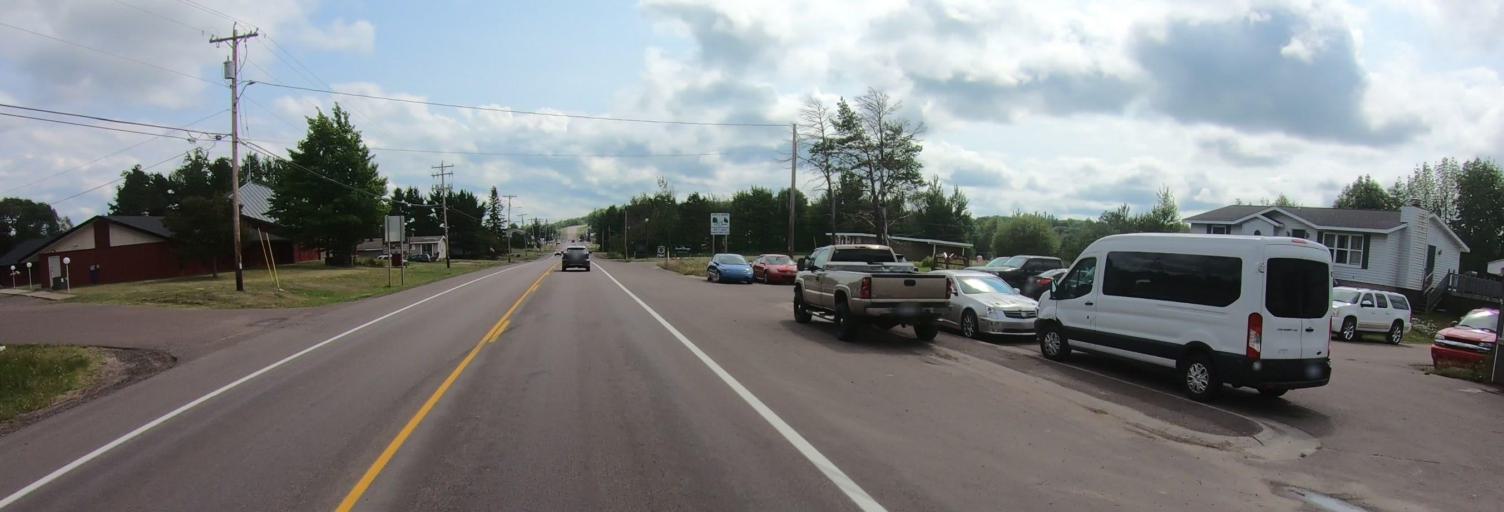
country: US
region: Michigan
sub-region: Houghton County
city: Hancock
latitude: 47.0763
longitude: -88.6405
